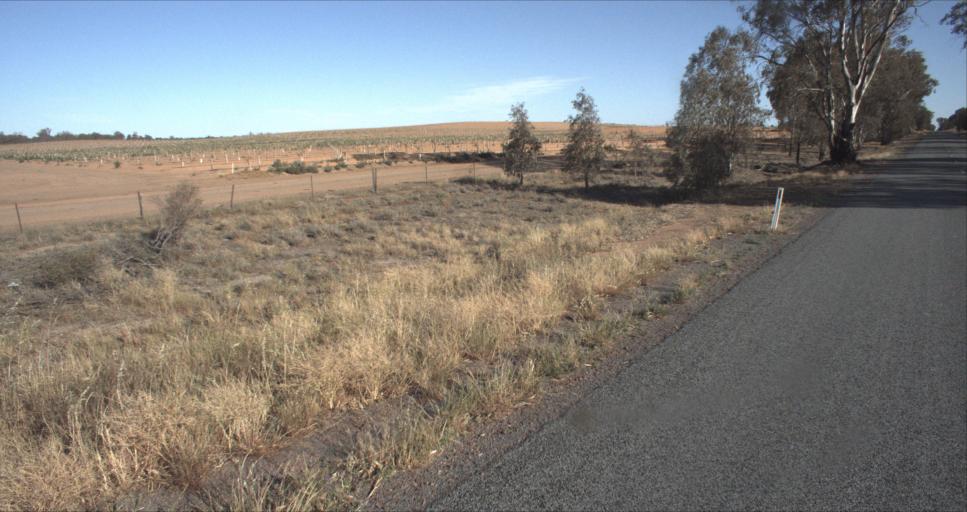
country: AU
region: New South Wales
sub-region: Leeton
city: Leeton
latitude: -34.6536
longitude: 146.3507
